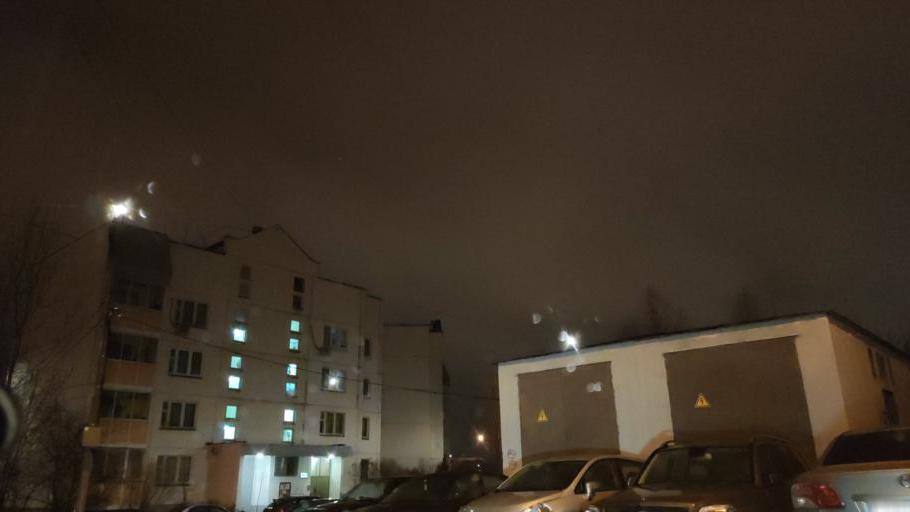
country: RU
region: Moskovskaya
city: Kommunarka
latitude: 55.5395
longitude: 37.5075
